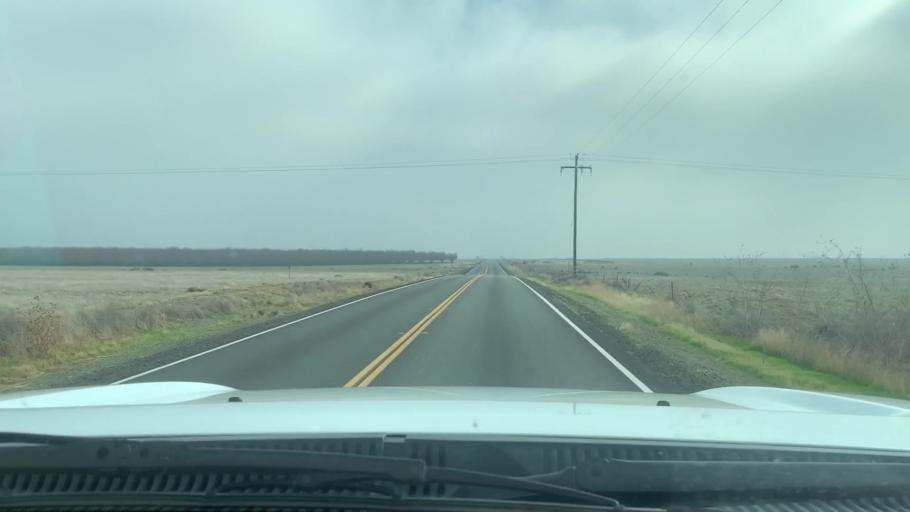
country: US
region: California
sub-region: Kern County
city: Lost Hills
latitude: 35.5595
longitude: -119.7995
